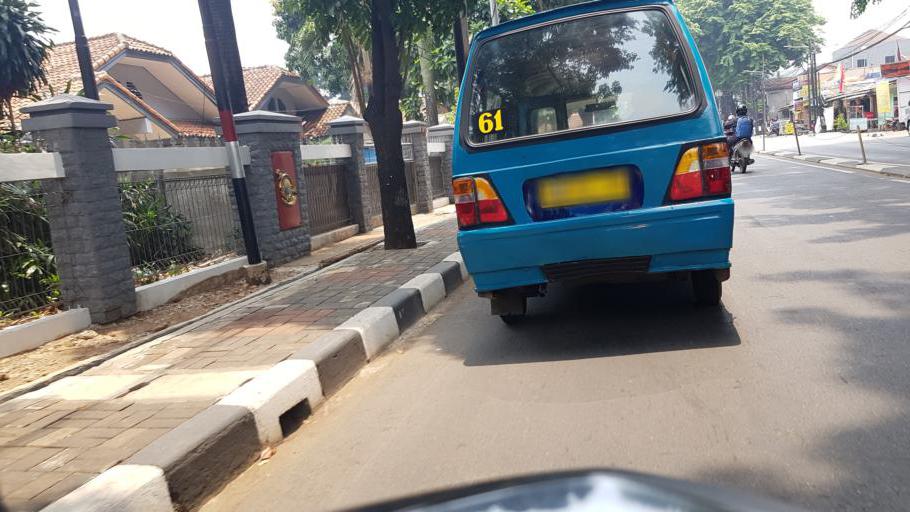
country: ID
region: West Java
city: Pamulang
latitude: -6.2990
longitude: 106.8146
